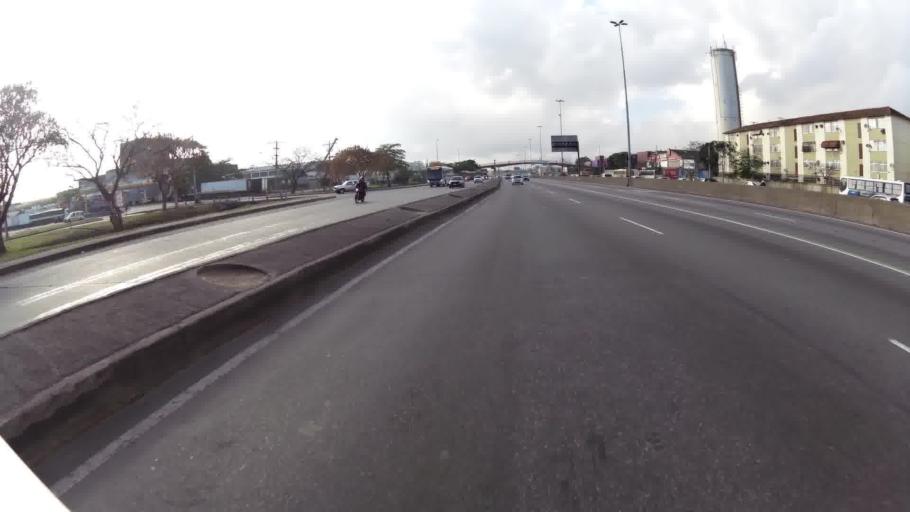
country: BR
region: Rio de Janeiro
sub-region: Duque De Caxias
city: Duque de Caxias
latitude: -22.8210
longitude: -43.2819
